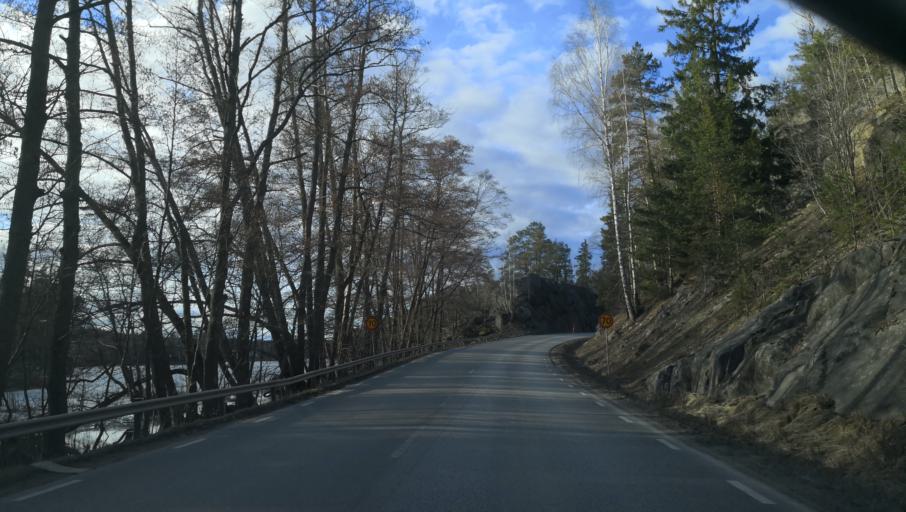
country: SE
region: Stockholm
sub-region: Varmdo Kommun
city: Gustavsberg
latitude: 59.3329
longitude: 18.3459
